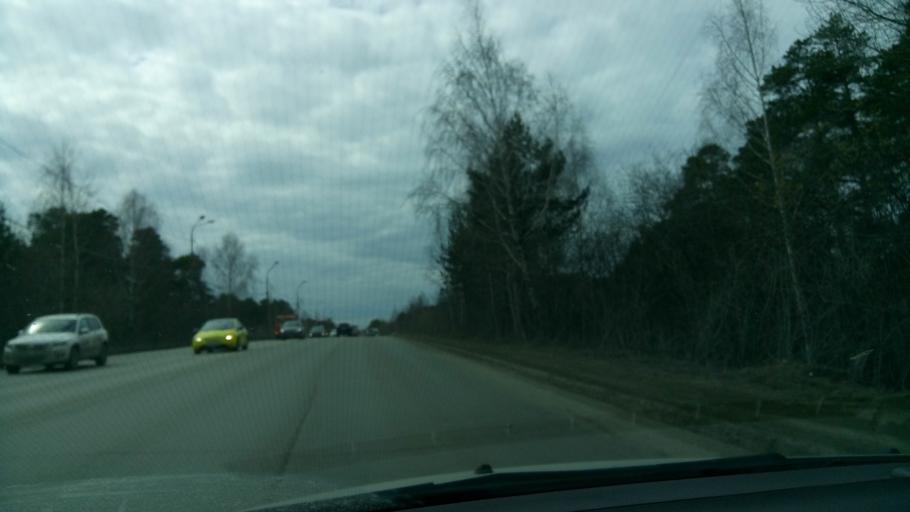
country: RU
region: Sverdlovsk
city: Beryozovsky
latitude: 56.8953
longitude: 60.7572
